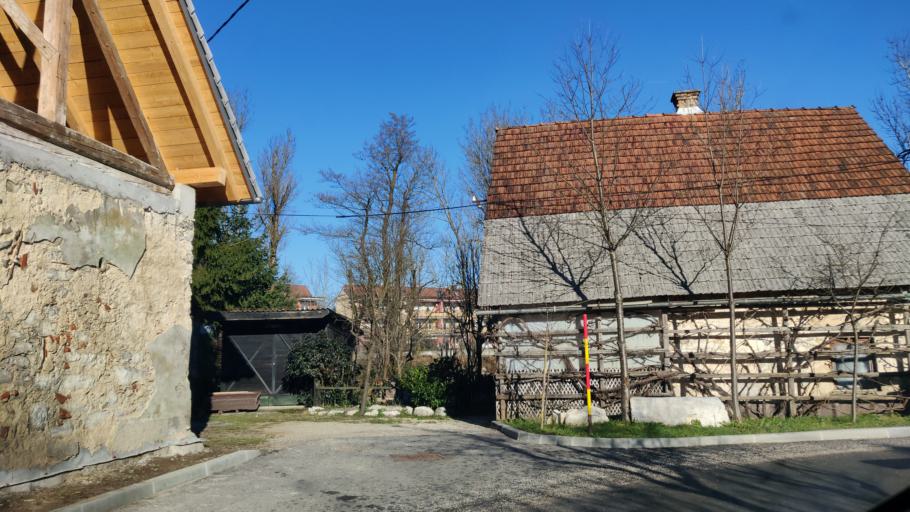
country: SI
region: Logatec
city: Logatec
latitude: 45.9151
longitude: 14.2232
